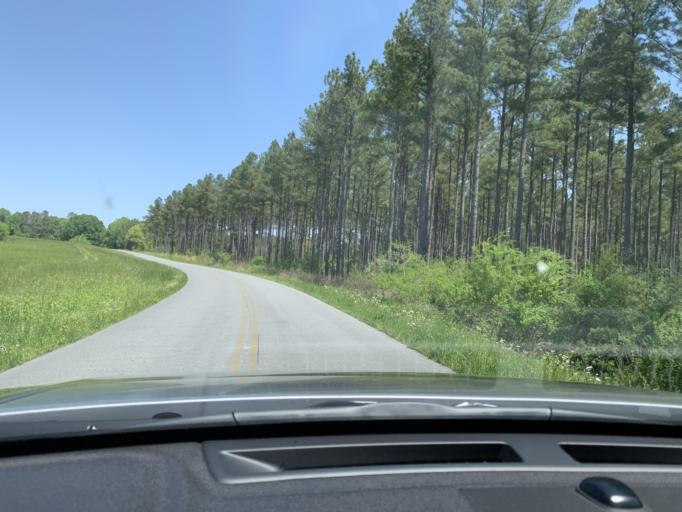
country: US
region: Georgia
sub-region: Polk County
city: Cedartown
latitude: 34.0509
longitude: -85.1844
